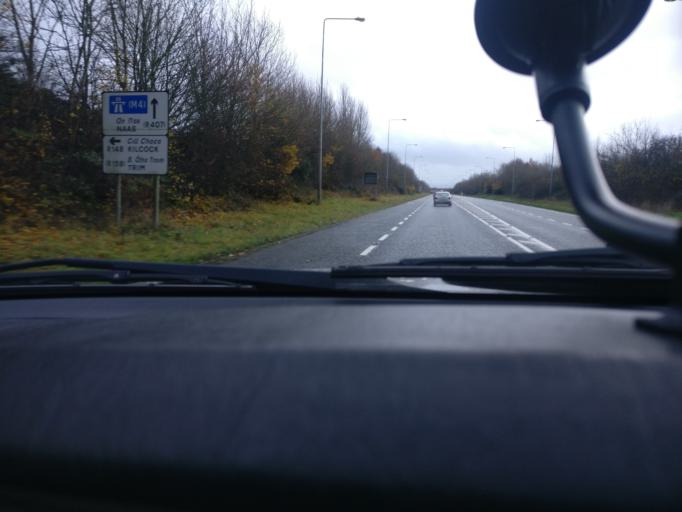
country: IE
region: Leinster
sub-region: Kildare
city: Kilcock
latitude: 53.4086
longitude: -6.7016
